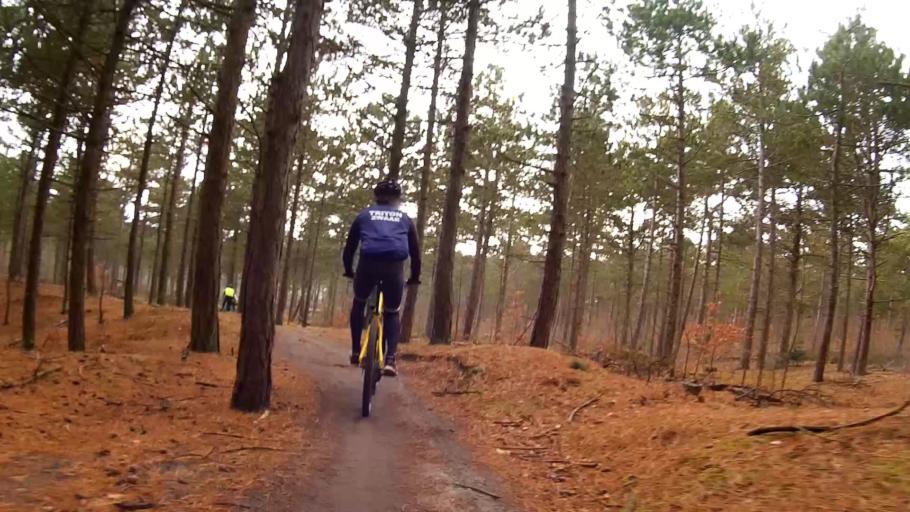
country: NL
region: North Holland
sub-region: Gemeente Bergen
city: Egmond aan Zee
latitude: 52.6929
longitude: 4.6647
